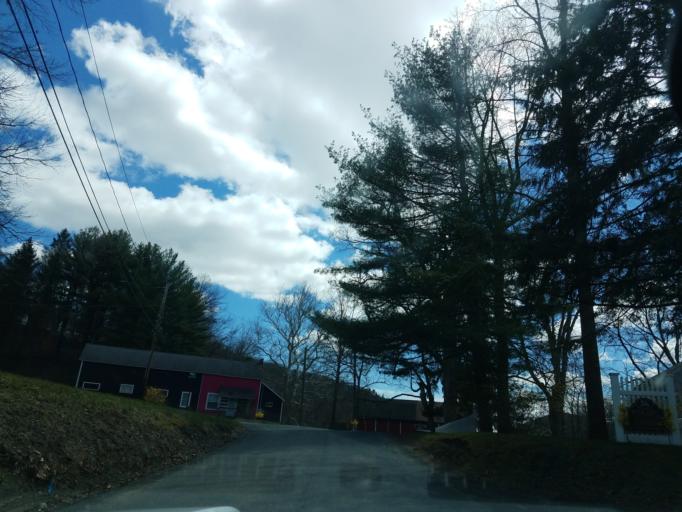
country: US
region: Connecticut
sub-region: Fairfield County
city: Sherman
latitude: 41.6458
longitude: -73.4790
